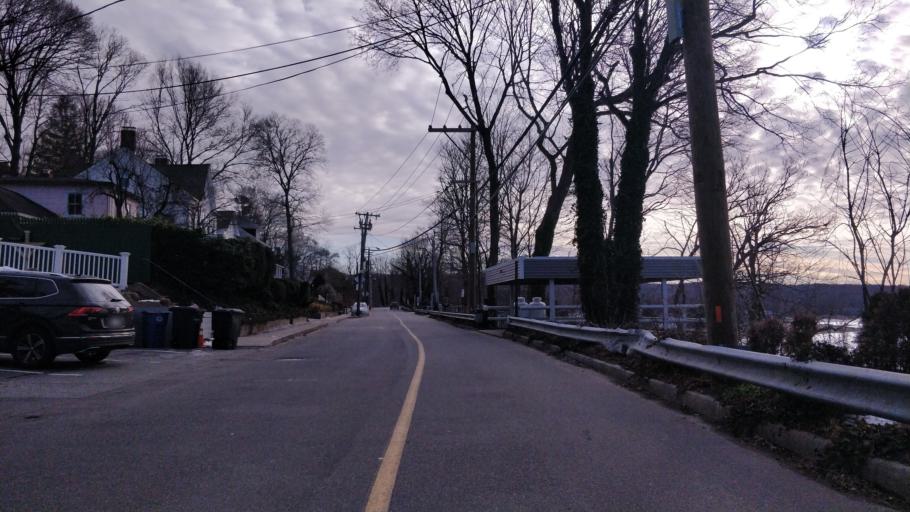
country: US
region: New York
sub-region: Suffolk County
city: Northport
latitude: 40.8971
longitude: -73.3527
